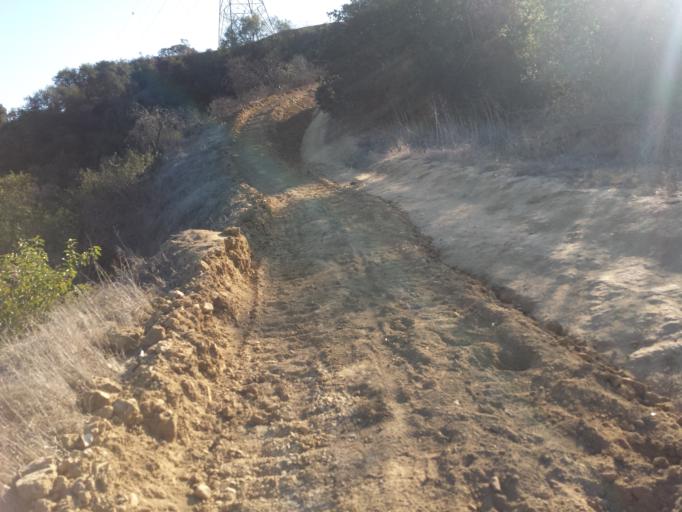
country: US
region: California
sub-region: Los Angeles County
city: Whittier
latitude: 34.0031
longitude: -118.0078
